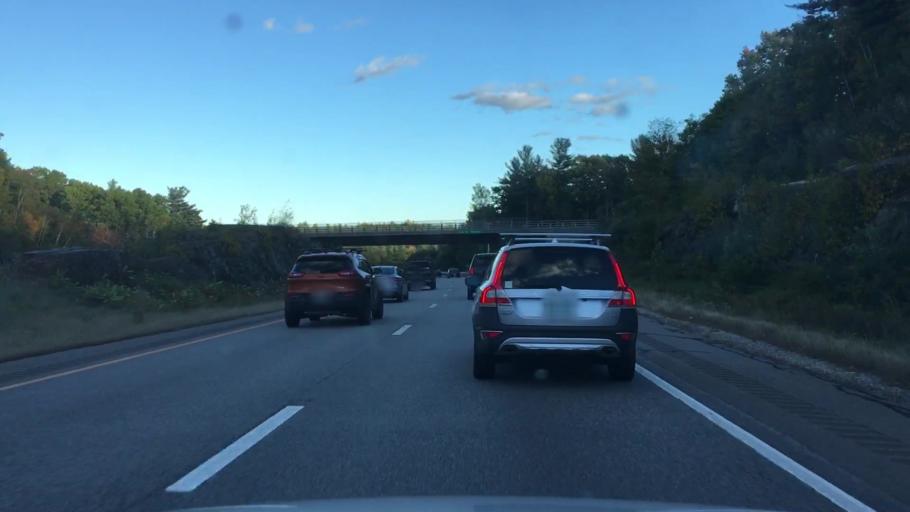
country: US
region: New Hampshire
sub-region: Rockingham County
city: Raymond
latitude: 43.0231
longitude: -71.2324
